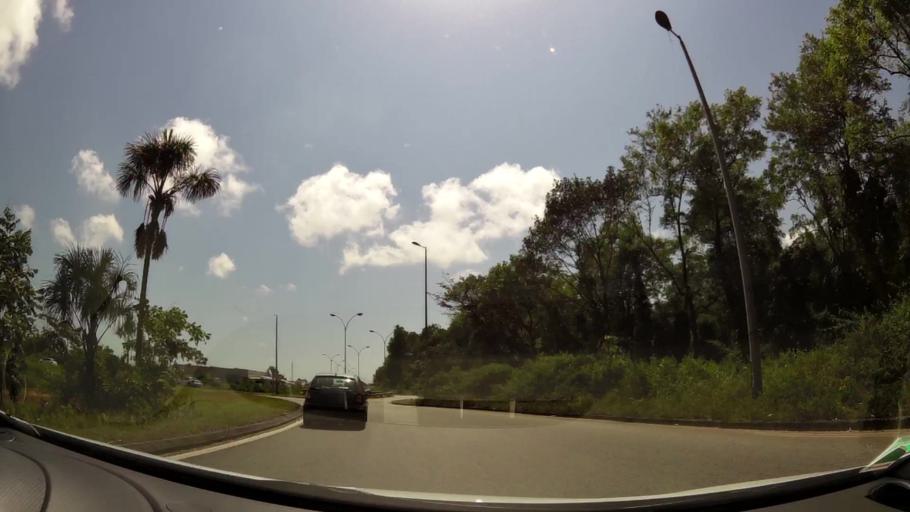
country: GF
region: Guyane
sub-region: Guyane
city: Cayenne
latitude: 4.9206
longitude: -52.3297
